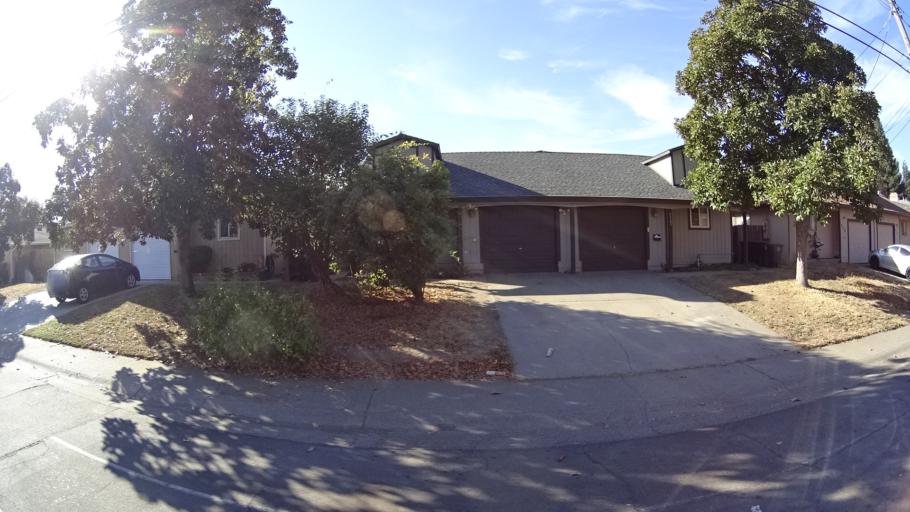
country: US
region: California
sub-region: Sacramento County
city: Antelope
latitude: 38.7041
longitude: -121.3155
